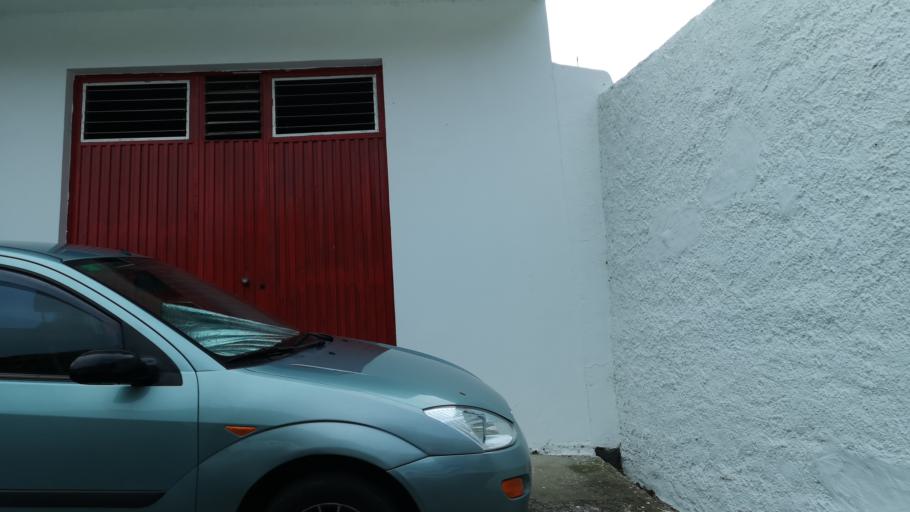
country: ES
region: Canary Islands
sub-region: Provincia de Santa Cruz de Tenerife
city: Vallehermosa
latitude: 28.1818
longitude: -17.2665
